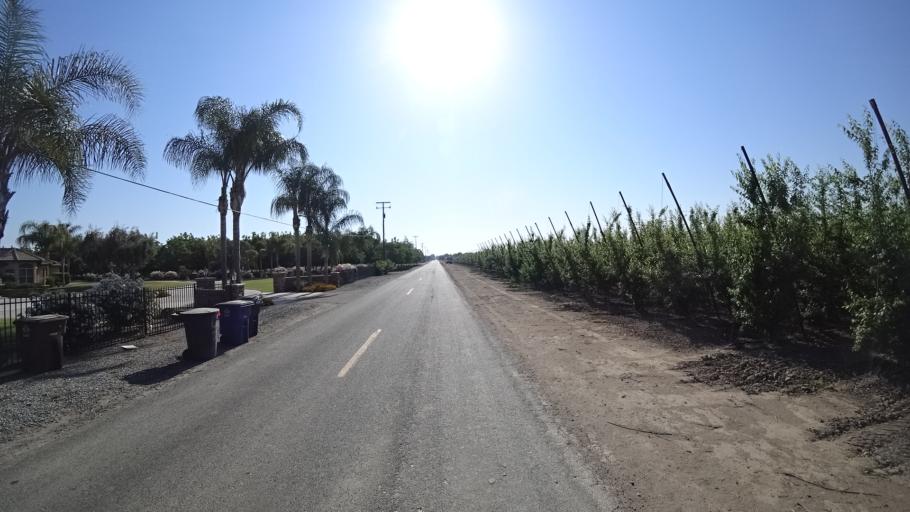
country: US
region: California
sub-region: Kings County
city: Lucerne
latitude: 36.3862
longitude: -119.6682
